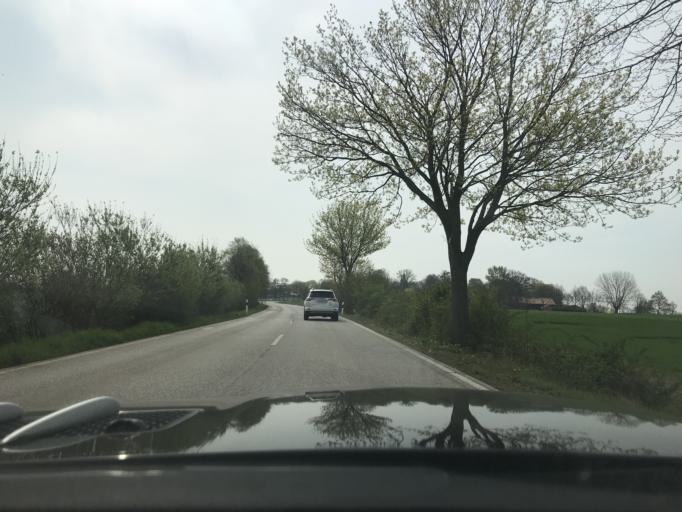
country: DE
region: Schleswig-Holstein
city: Heringsdorf
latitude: 54.2929
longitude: 11.0149
